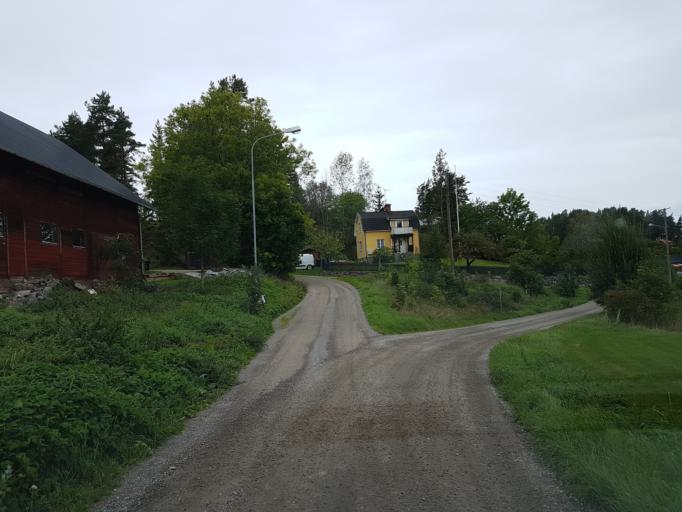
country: SE
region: OEstergoetland
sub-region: Atvidabergs Kommun
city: Atvidaberg
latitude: 58.2156
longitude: 16.0313
